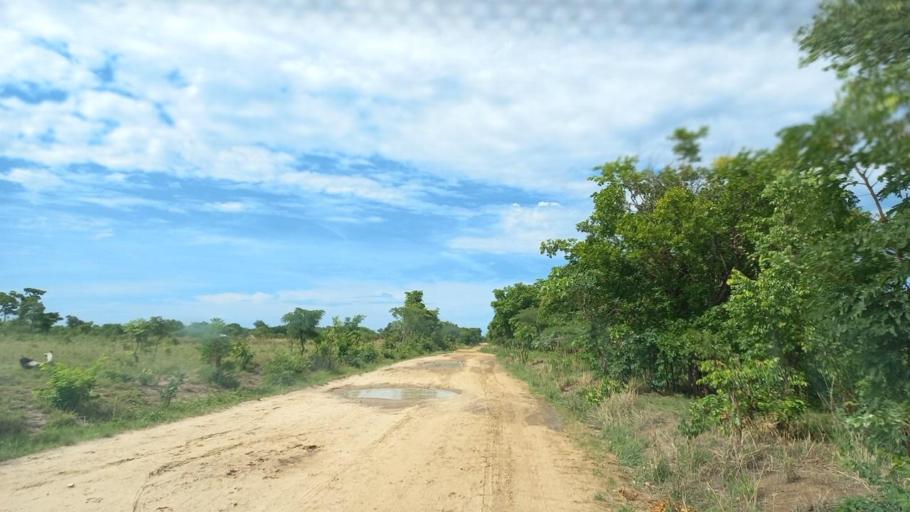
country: ZM
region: North-Western
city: Kabompo
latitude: -13.5179
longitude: 24.3872
